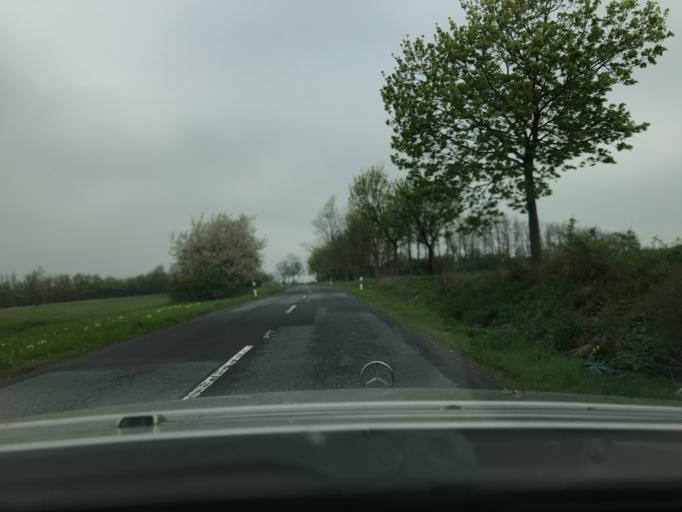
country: DE
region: Thuringia
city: Kefferhausen
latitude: 51.3286
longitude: 10.2697
